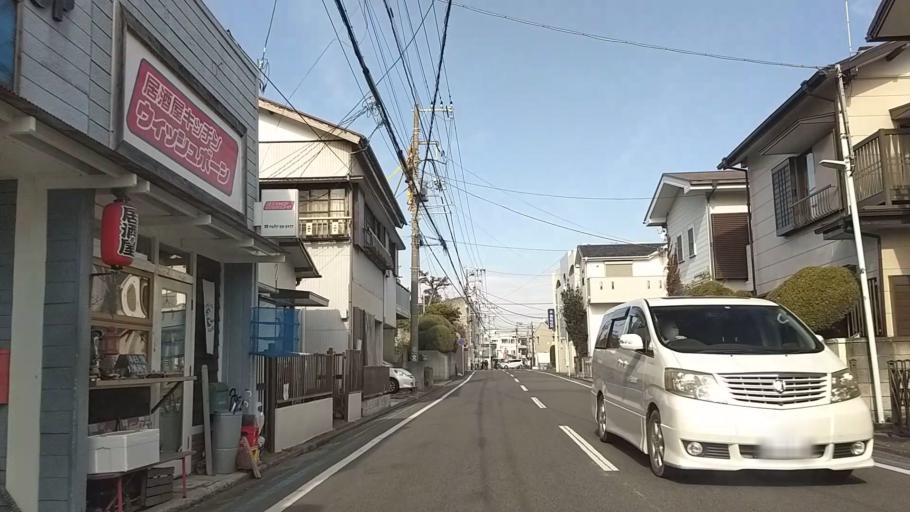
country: JP
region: Kanagawa
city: Chigasaki
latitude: 35.3232
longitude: 139.4009
